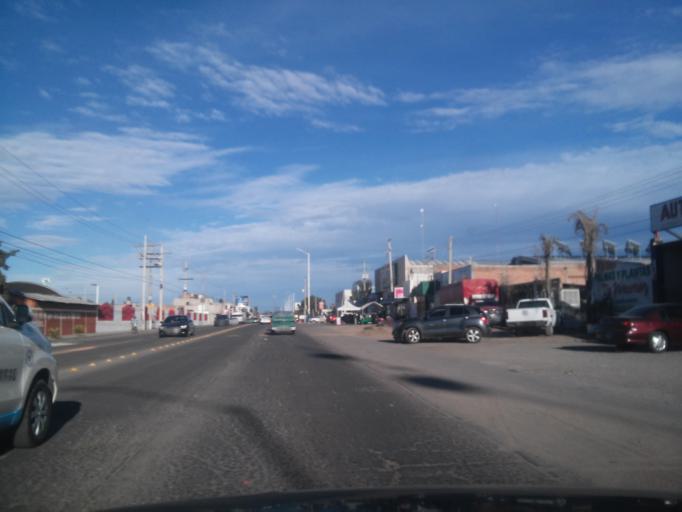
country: MX
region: Durango
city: Victoria de Durango
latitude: 24.0041
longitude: -104.6493
